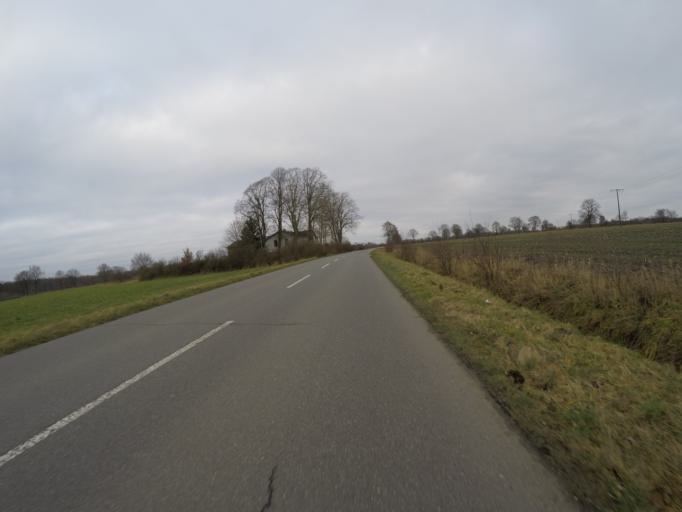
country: DE
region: Schleswig-Holstein
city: Langeln
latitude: 53.7886
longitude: 9.8369
